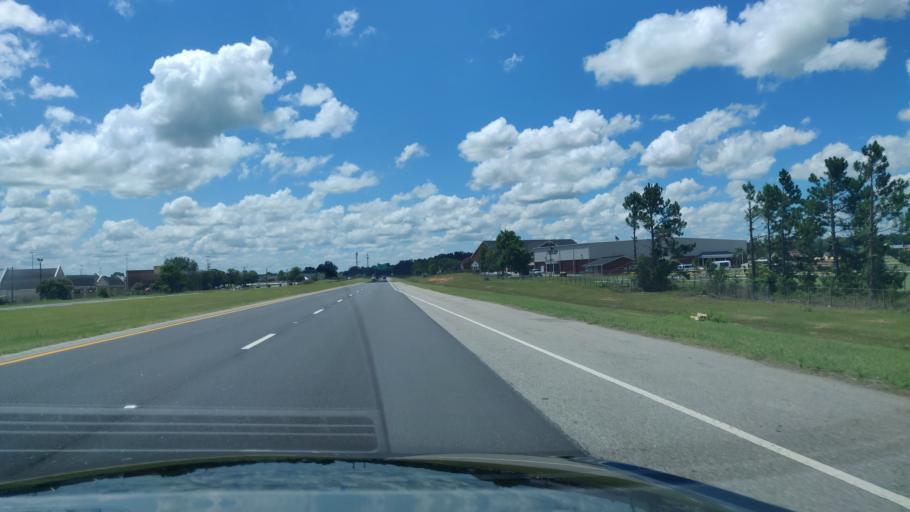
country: US
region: Georgia
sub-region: Dougherty County
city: Albany
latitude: 31.6199
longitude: -84.2123
